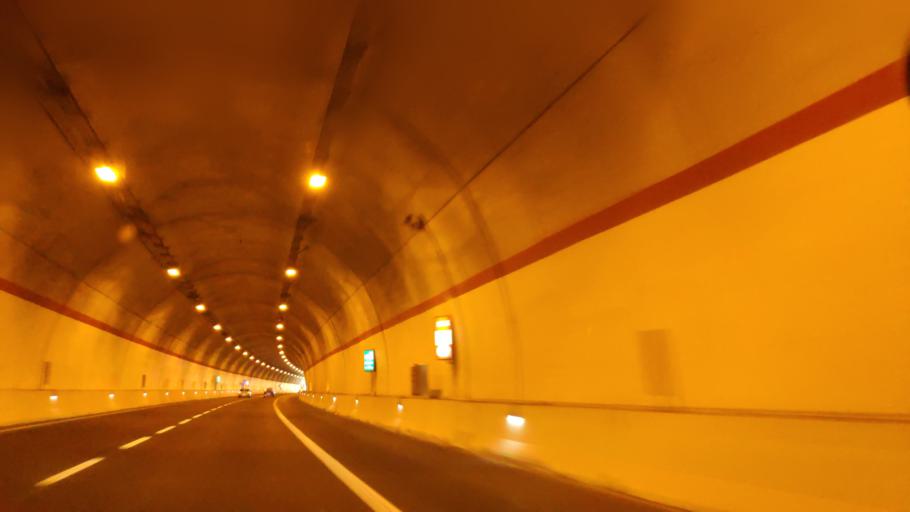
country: IT
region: Basilicate
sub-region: Provincia di Potenza
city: Castelluccio Superiore
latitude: 40.0090
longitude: 15.9043
